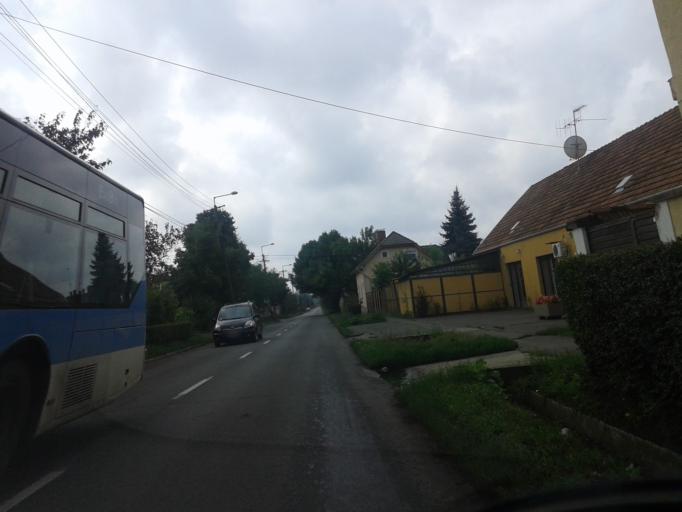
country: HU
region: Csongrad
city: Szeged
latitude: 46.2664
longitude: 20.1783
